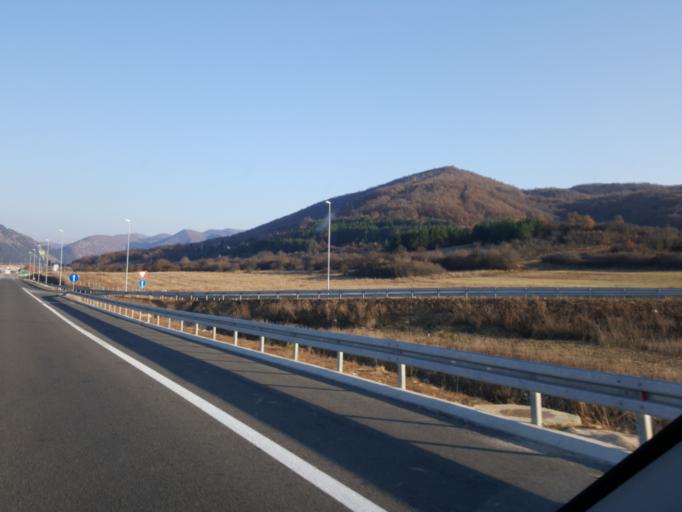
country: RS
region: Central Serbia
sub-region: Pirotski Okrug
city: Dimitrovgrad
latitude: 43.0018
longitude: 22.8126
